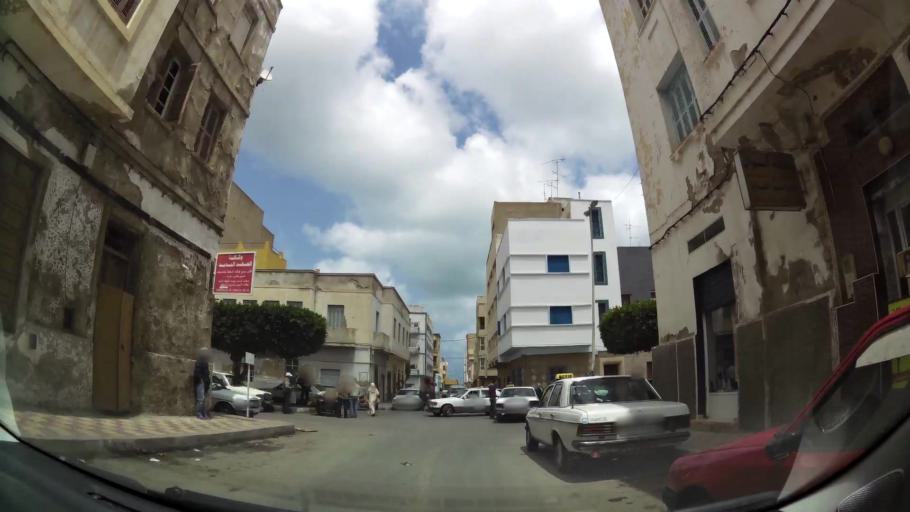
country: MA
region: Oriental
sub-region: Nador
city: Nador
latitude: 35.1804
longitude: -2.9258
